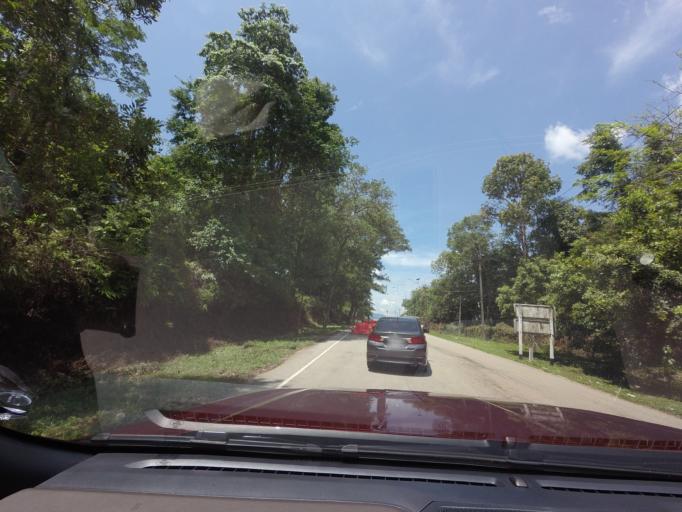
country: TH
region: Narathiwat
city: Chanae
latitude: 6.1828
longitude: 101.6969
